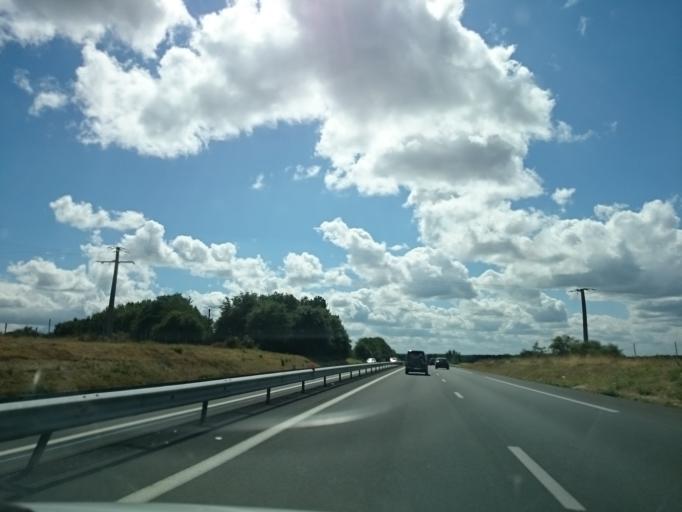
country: FR
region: Pays de la Loire
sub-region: Departement de la Sarthe
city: Vion
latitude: 47.7538
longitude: -0.2362
